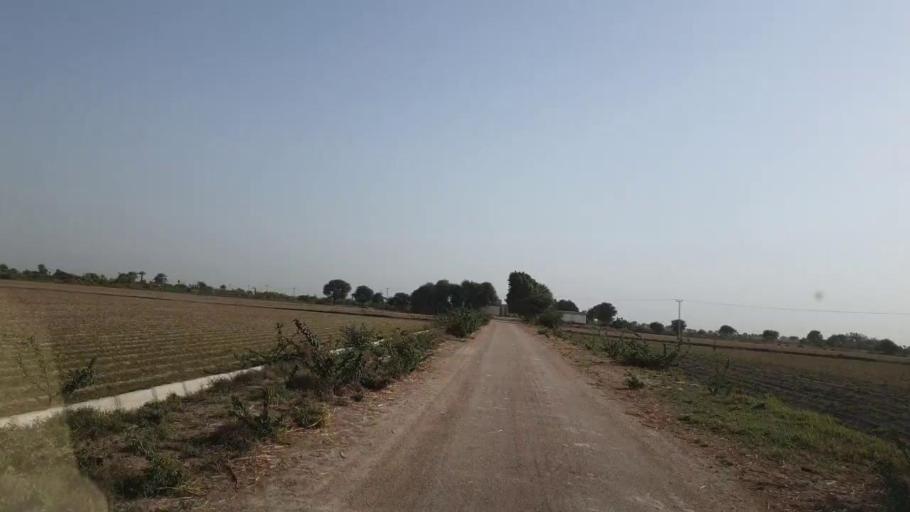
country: PK
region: Sindh
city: Tando Ghulam Ali
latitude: 25.0874
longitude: 68.8530
